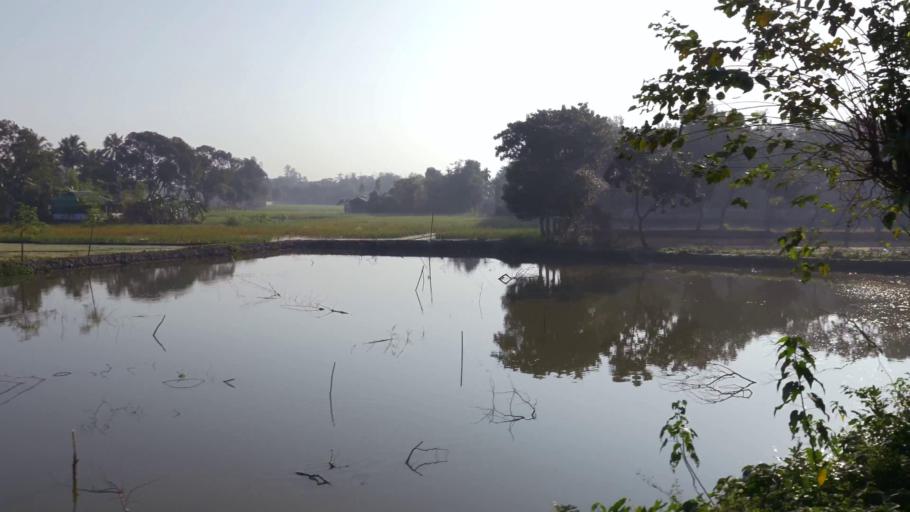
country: BD
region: Dhaka
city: Jamalpur
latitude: 24.9057
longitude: 89.9702
